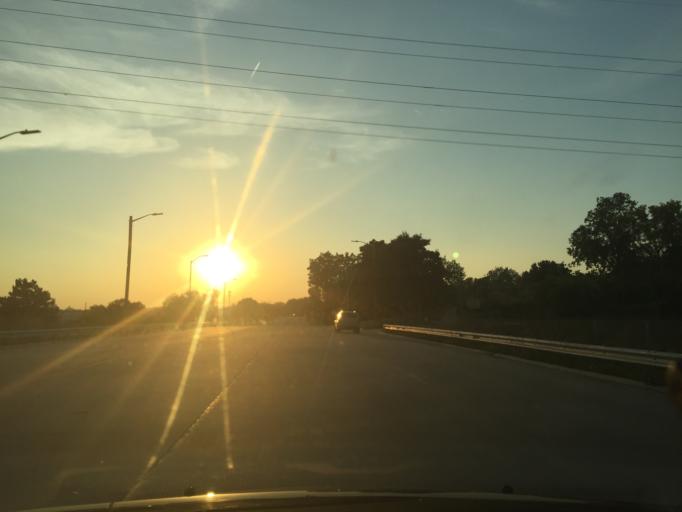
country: US
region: Michigan
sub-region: Oakland County
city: Pontiac
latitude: 42.6488
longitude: -83.2586
